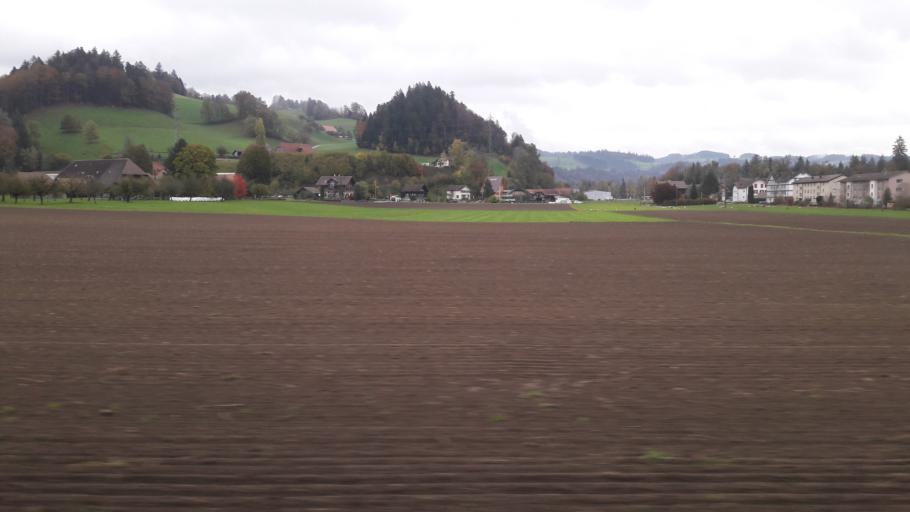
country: CH
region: Bern
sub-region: Emmental District
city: Lutzelfluh
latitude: 46.9988
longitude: 7.7054
